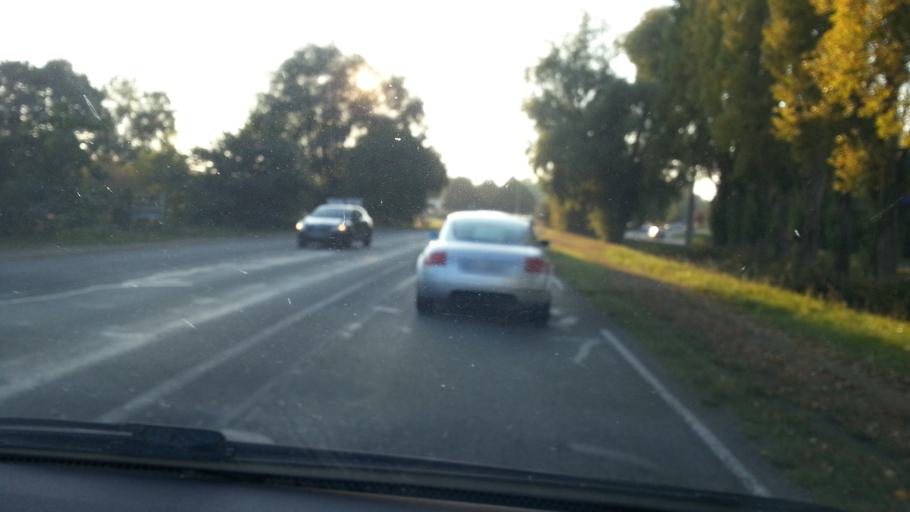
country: FR
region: Picardie
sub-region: Departement de l'Oise
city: Villers-Saint-Paul
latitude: 49.2844
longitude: 2.4911
